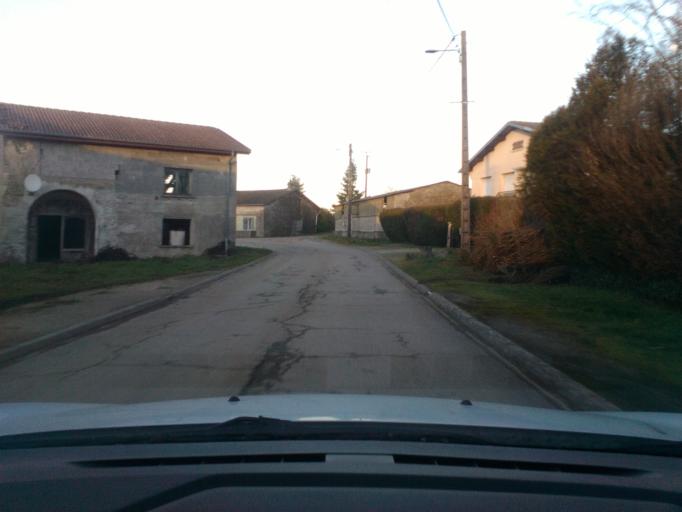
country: FR
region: Lorraine
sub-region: Departement des Vosges
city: Vittel
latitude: 48.3092
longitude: 5.9948
